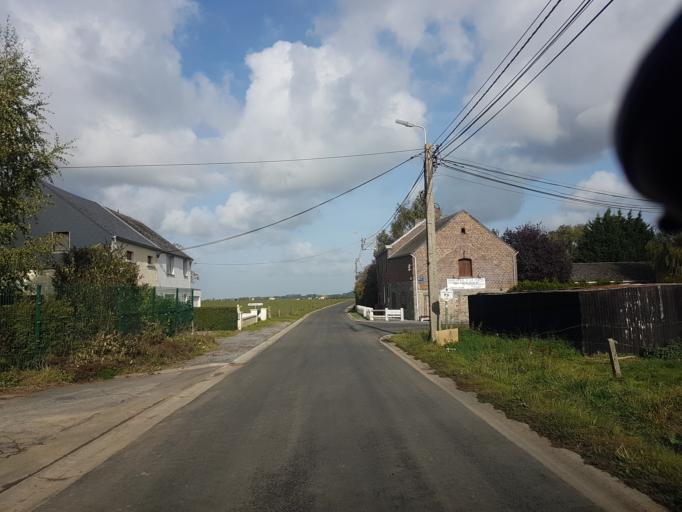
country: BE
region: Wallonia
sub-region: Province de Liege
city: Heron
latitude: 50.5546
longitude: 5.0957
